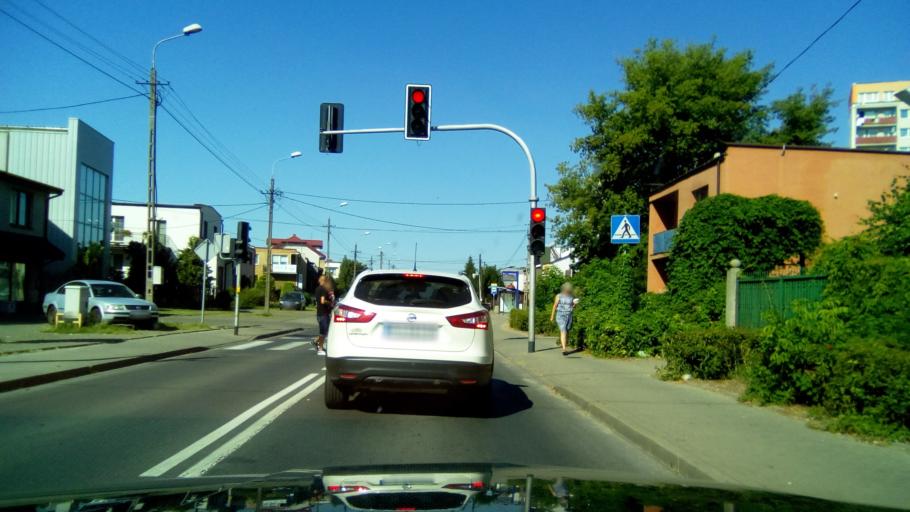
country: PL
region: Masovian Voivodeship
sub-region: Plock
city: Plock
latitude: 52.5390
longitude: 19.7302
